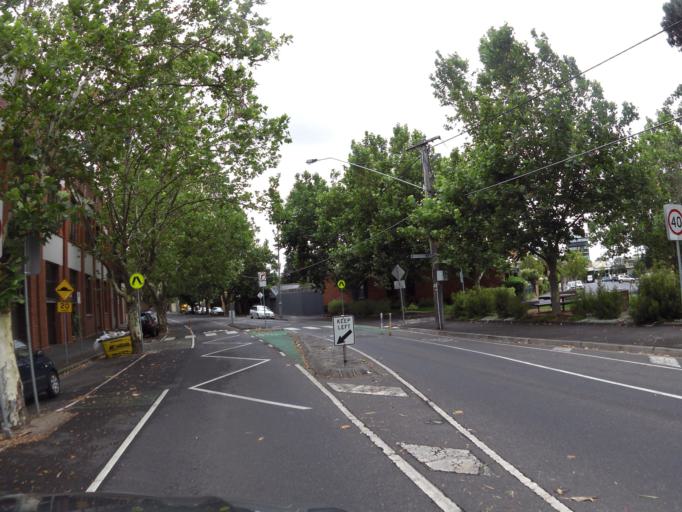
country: AU
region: Victoria
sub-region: Yarra
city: Clifton Hill
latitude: -37.7980
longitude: 144.9980
